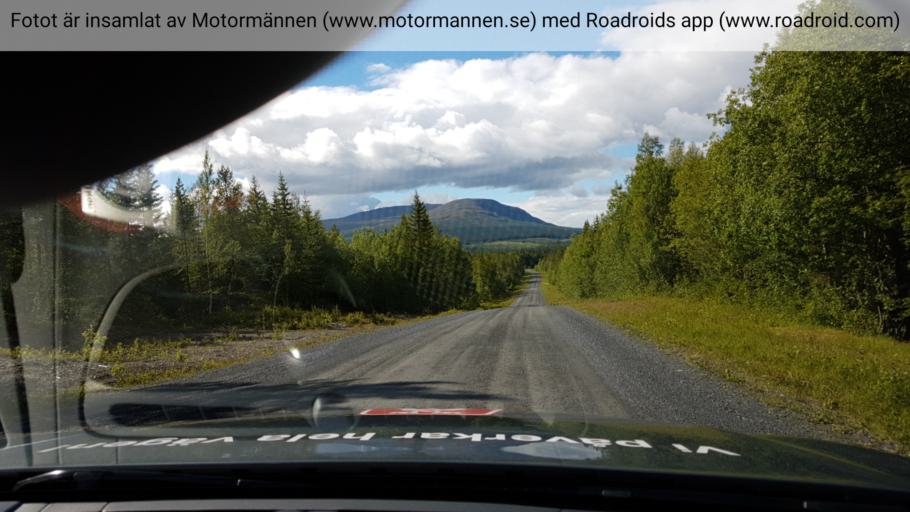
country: SE
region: Jaemtland
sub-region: Krokoms Kommun
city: Valla
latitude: 63.0894
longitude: 13.9064
